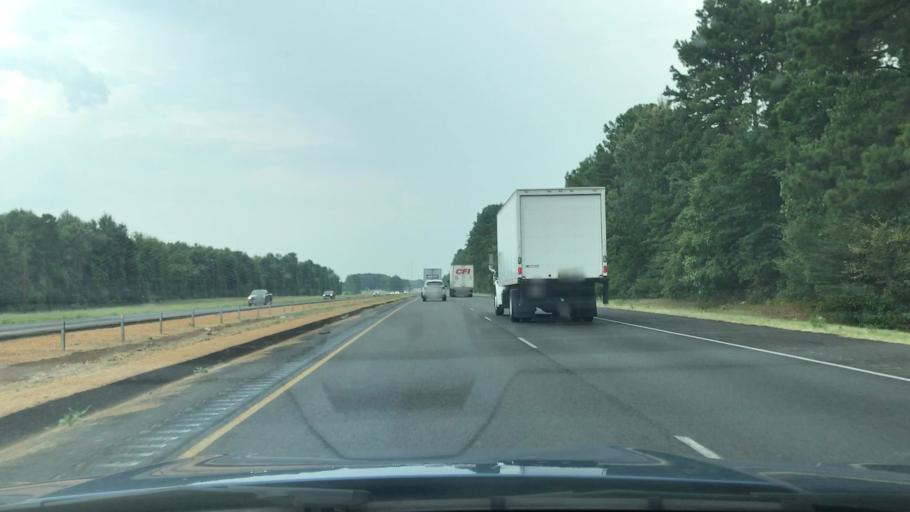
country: US
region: Texas
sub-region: Harrison County
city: Marshall
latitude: 32.4953
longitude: -94.2540
